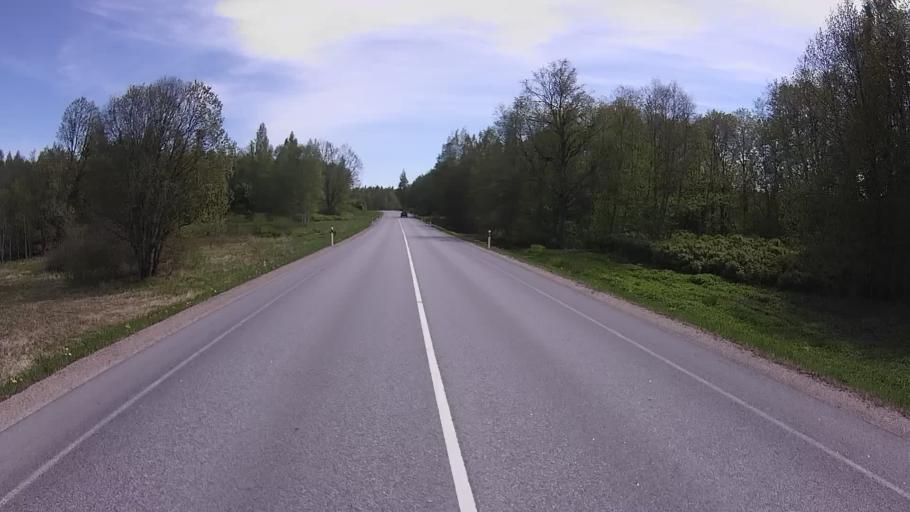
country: EE
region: Valgamaa
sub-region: Valga linn
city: Valga
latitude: 57.7173
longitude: 26.2023
